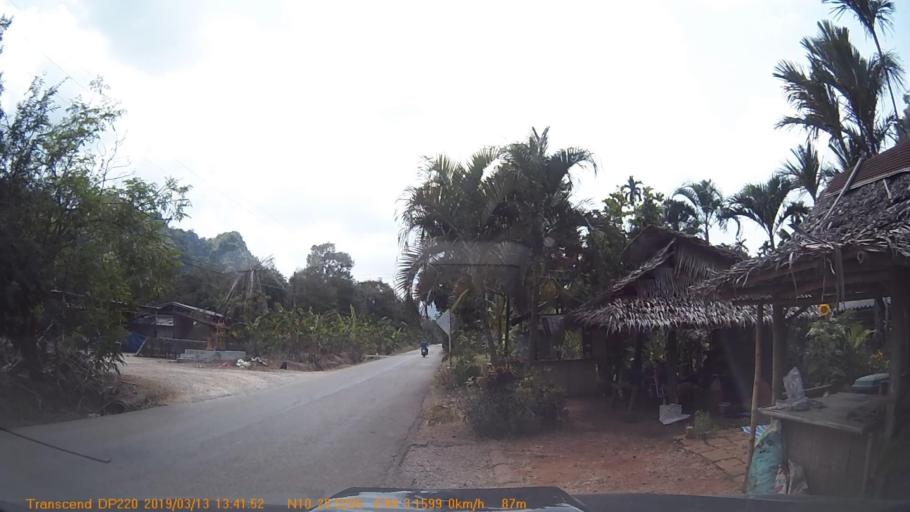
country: TH
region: Chumphon
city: Chumphon
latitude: 10.4259
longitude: 99.0534
